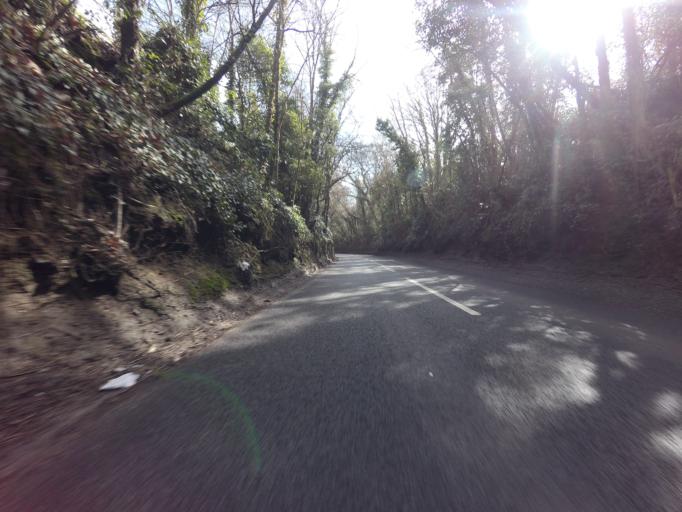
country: GB
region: England
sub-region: Greater London
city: Orpington
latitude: 51.3863
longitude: 0.1340
